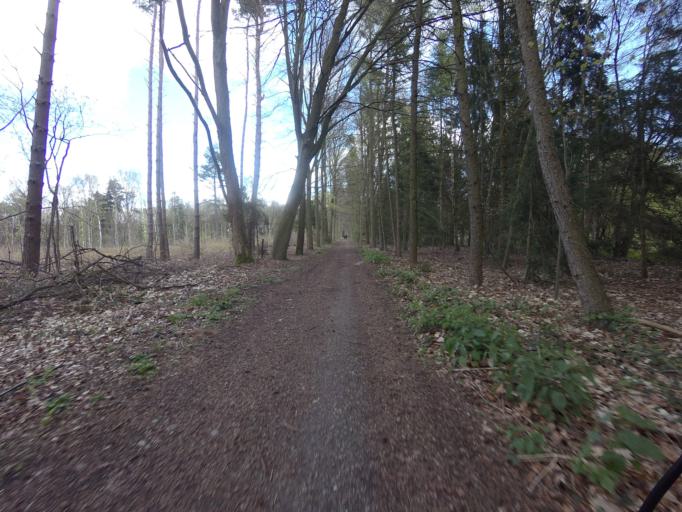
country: BE
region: Flanders
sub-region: Provincie Vlaams-Brabant
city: Kampenhout
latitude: 50.9726
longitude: 4.5165
